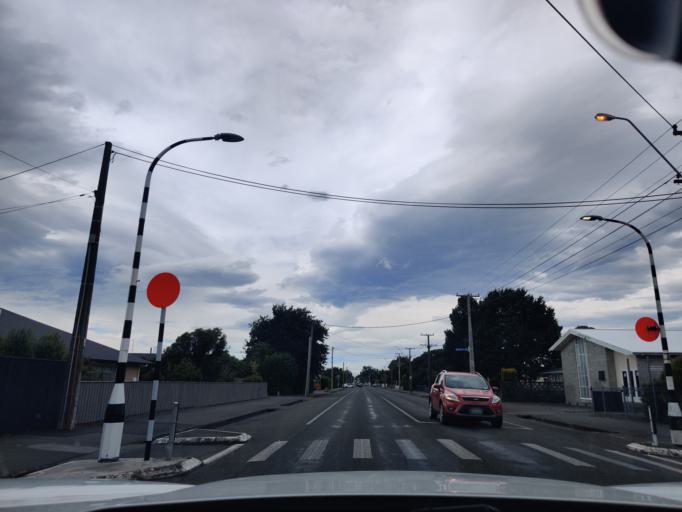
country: NZ
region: Wellington
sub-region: Masterton District
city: Masterton
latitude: -41.0337
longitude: 175.5189
